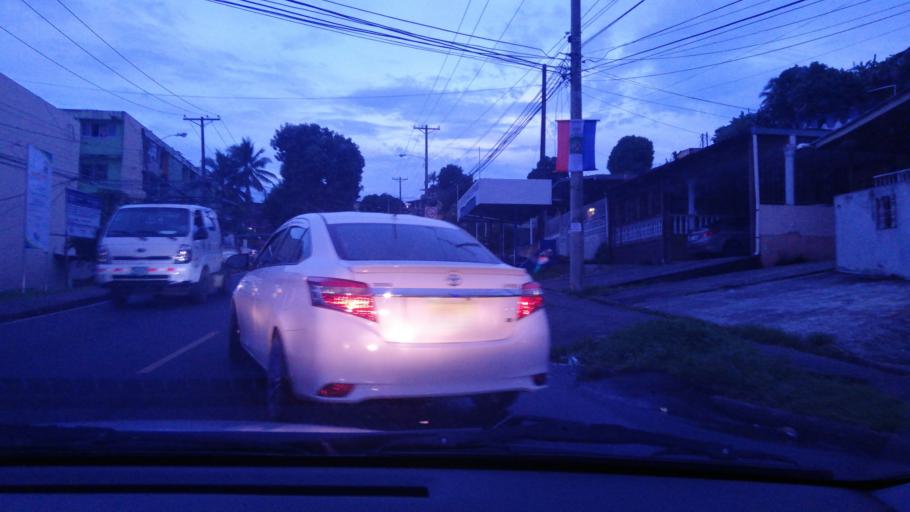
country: PA
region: Panama
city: San Miguelito
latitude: 9.0330
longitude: -79.4922
